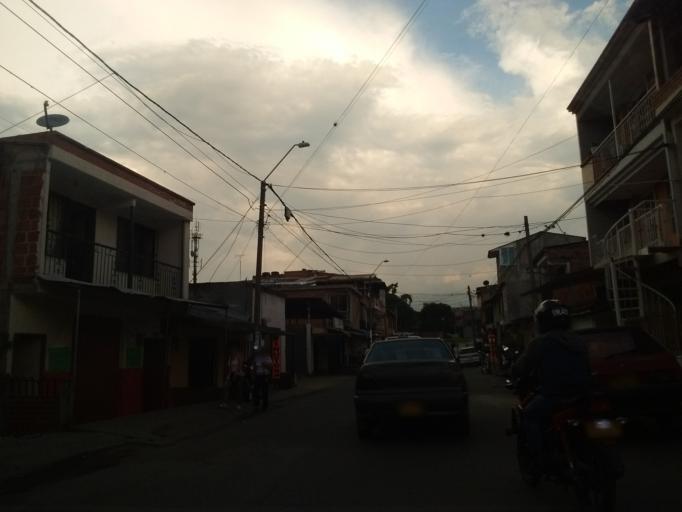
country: CO
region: Cauca
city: Santander de Quilichao
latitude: 3.0168
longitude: -76.4814
